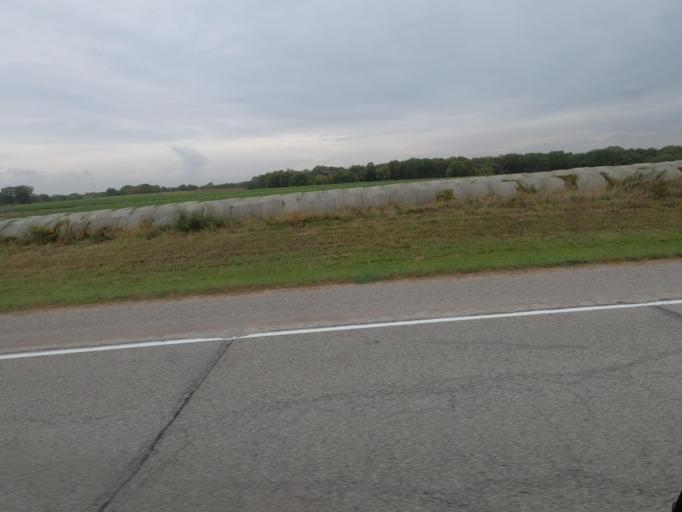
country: US
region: Iowa
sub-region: Van Buren County
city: Keosauqua
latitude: 40.8505
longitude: -92.0411
